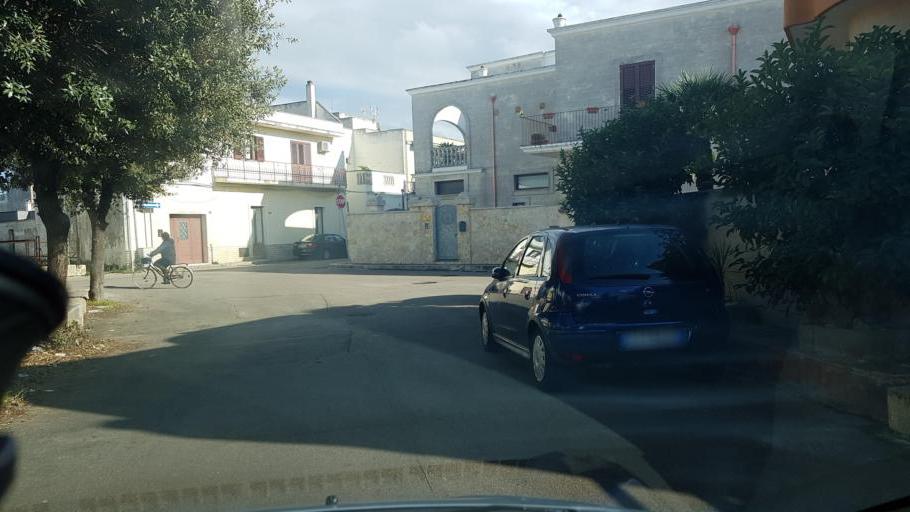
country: IT
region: Apulia
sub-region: Provincia di Brindisi
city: San Pietro Vernotico
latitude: 40.4851
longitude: 17.9918
